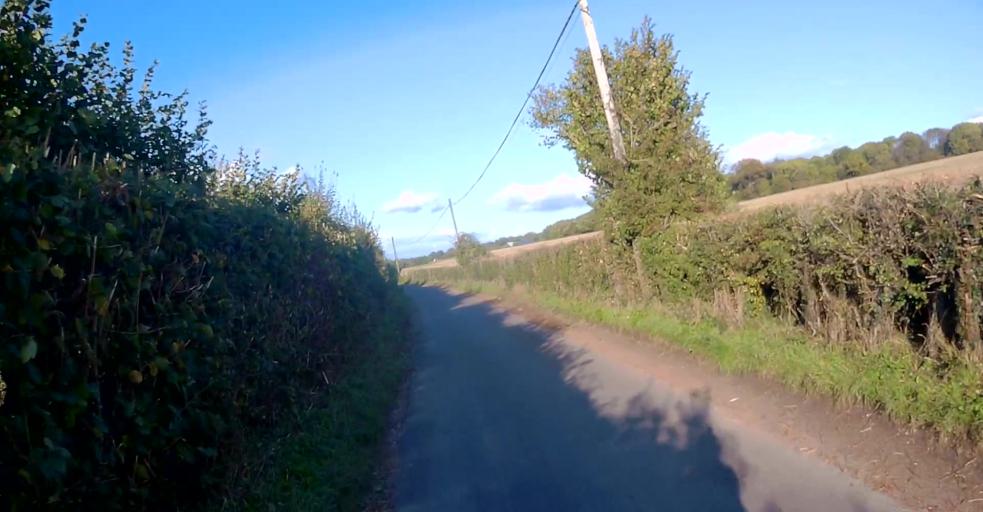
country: GB
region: England
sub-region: Hampshire
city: Long Sutton
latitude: 51.2184
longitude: -0.9216
